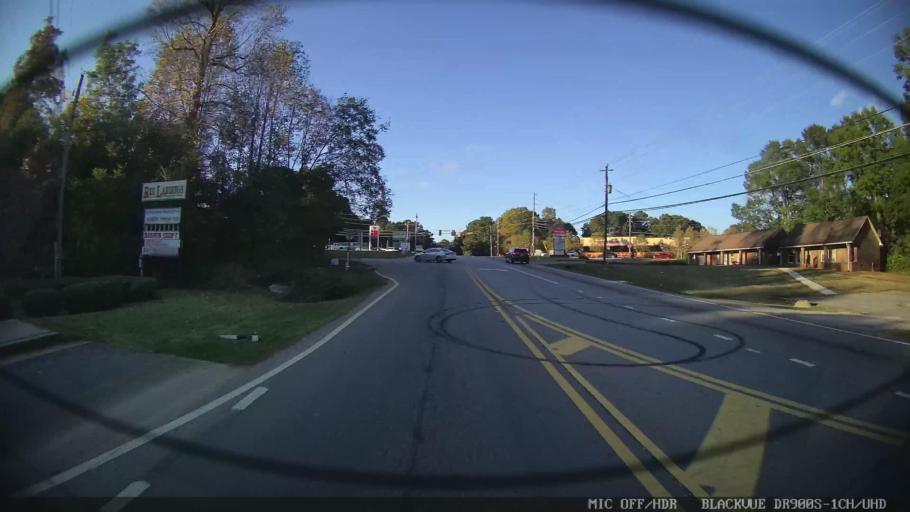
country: US
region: Georgia
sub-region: Clayton County
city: Lake City
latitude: 33.5908
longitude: -84.2939
